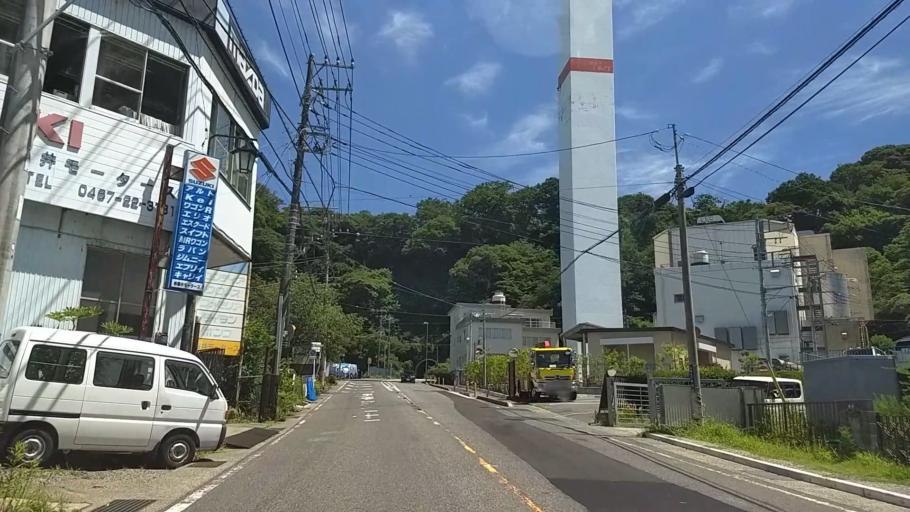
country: JP
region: Kanagawa
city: Kamakura
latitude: 35.3089
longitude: 139.5607
